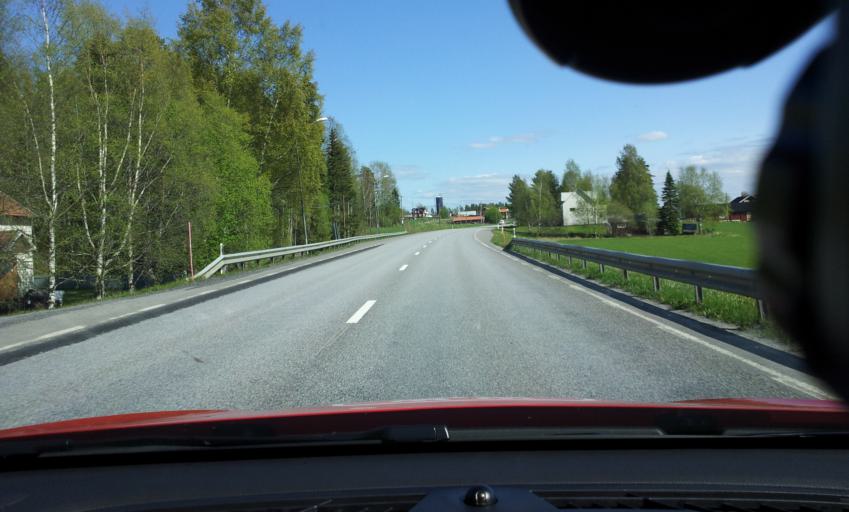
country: SE
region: Jaemtland
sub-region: Krokoms Kommun
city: Valla
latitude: 63.3186
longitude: 14.0803
